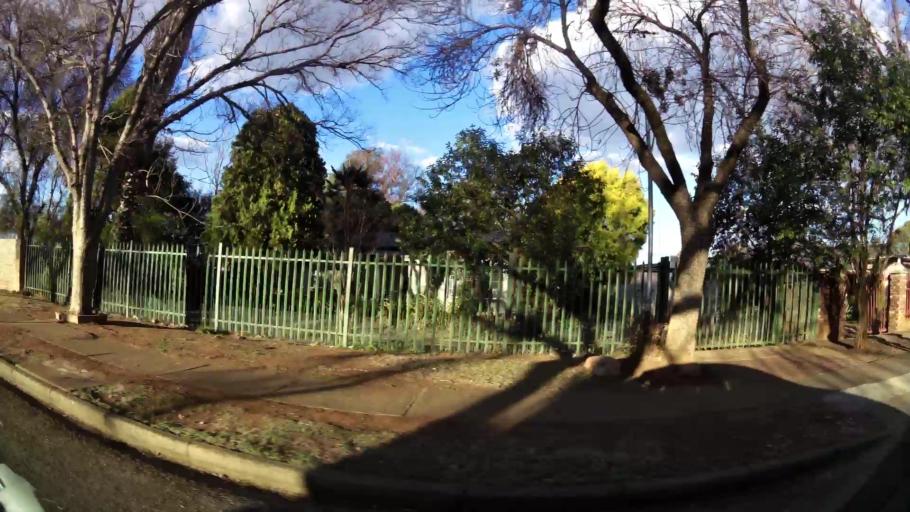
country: ZA
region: North-West
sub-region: Dr Kenneth Kaunda District Municipality
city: Potchefstroom
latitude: -26.7193
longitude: 27.1007
